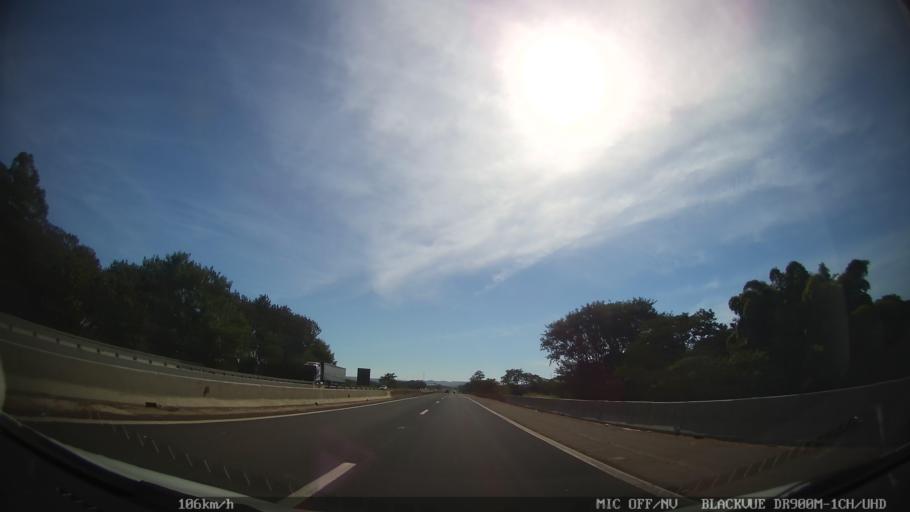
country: BR
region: Sao Paulo
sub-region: Porto Ferreira
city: Porto Ferreira
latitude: -21.8439
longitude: -47.4952
